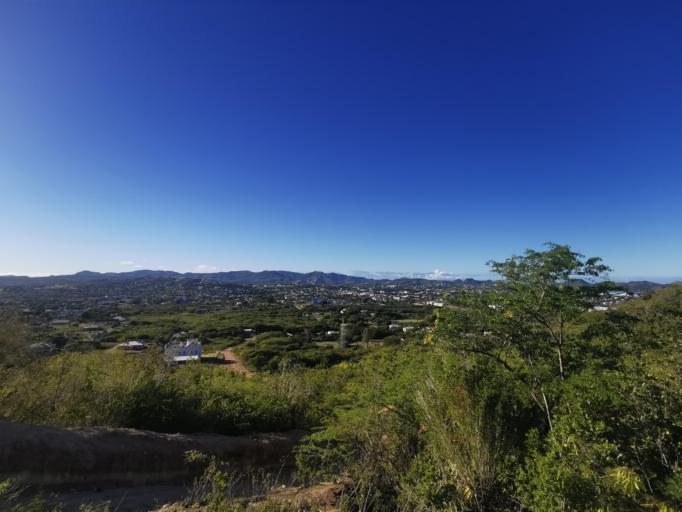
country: AG
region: Saint John
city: Saint John's
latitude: 17.1382
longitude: -61.8239
